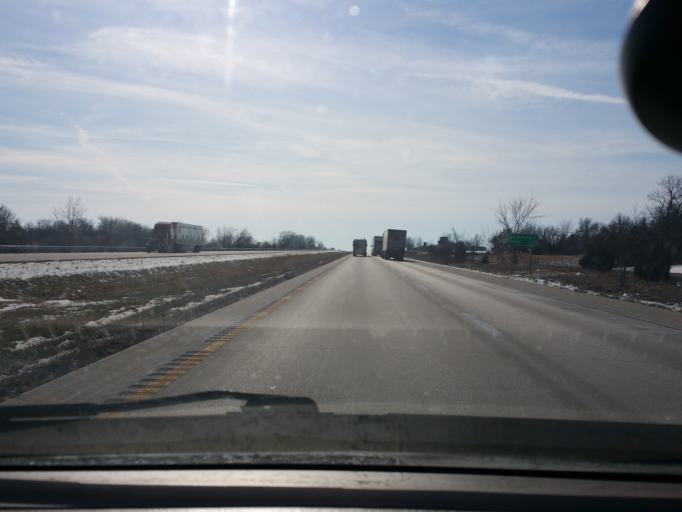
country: US
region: Missouri
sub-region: Clinton County
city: Cameron
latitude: 39.6543
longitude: -94.2392
